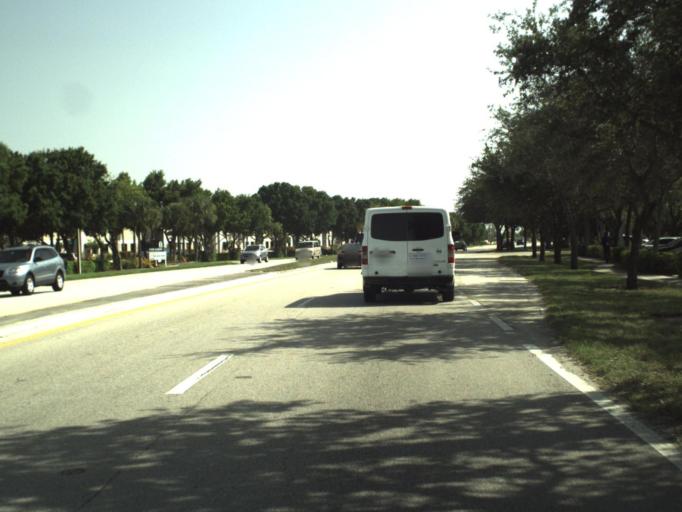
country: US
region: Florida
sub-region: Broward County
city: Tedder
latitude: 26.2709
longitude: -80.1361
